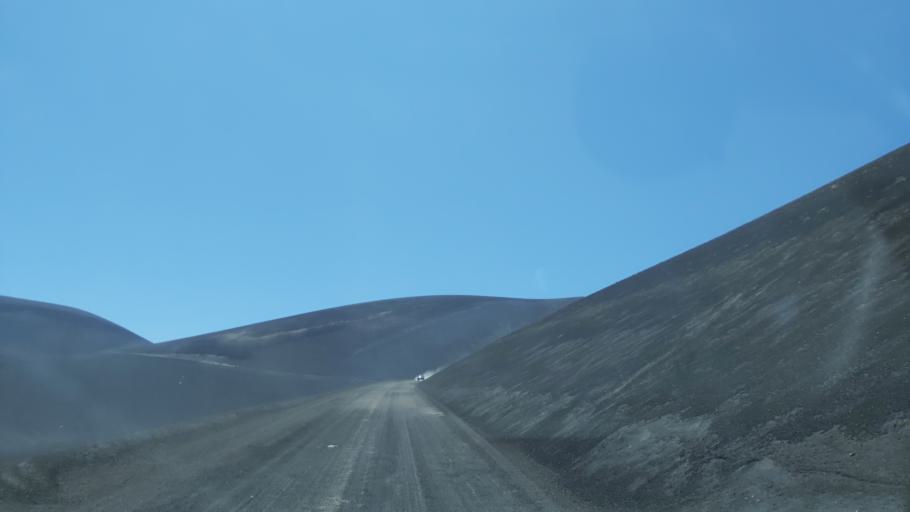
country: CL
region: Araucania
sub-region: Provincia de Cautin
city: Vilcun
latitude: -38.3938
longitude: -71.5457
